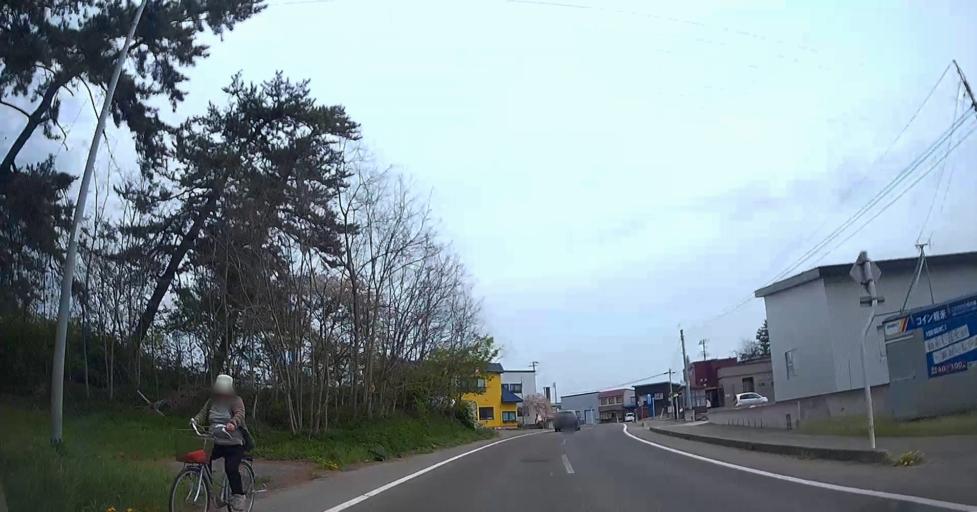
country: JP
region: Aomori
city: Shimokizukuri
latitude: 40.9700
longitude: 140.3668
